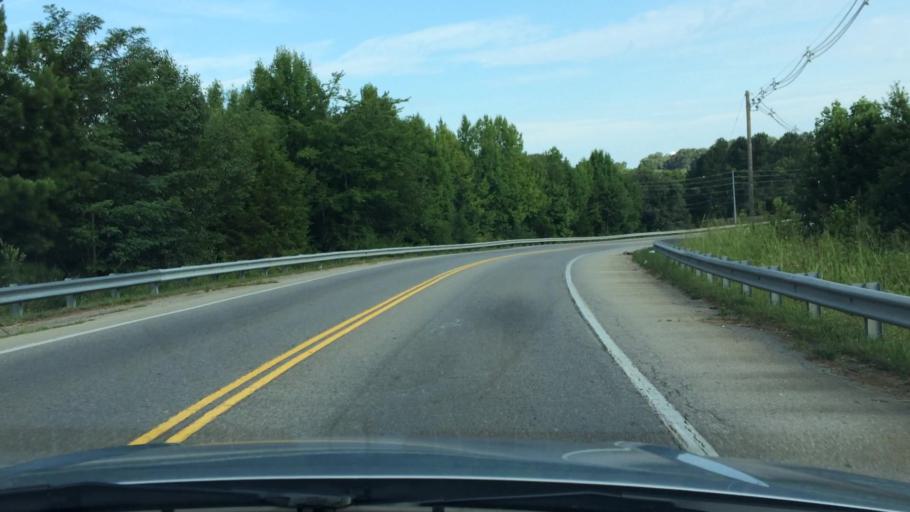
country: US
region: Tennessee
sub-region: Blount County
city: Maryville
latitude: 35.7417
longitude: -84.0433
